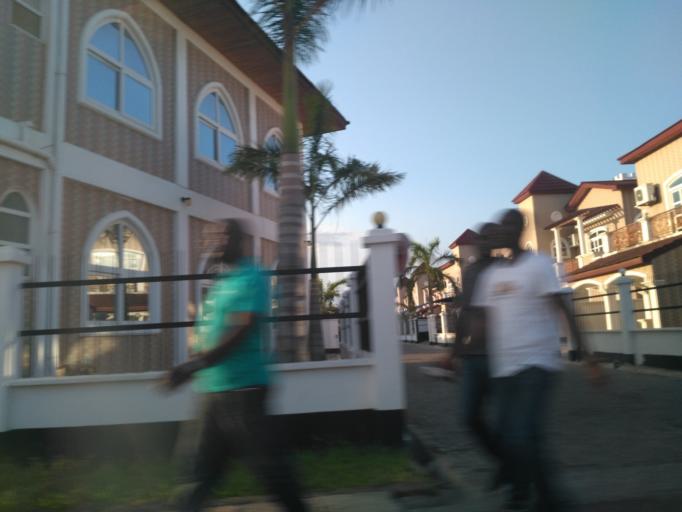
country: TZ
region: Dar es Salaam
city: Magomeni
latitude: -6.7662
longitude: 39.2616
